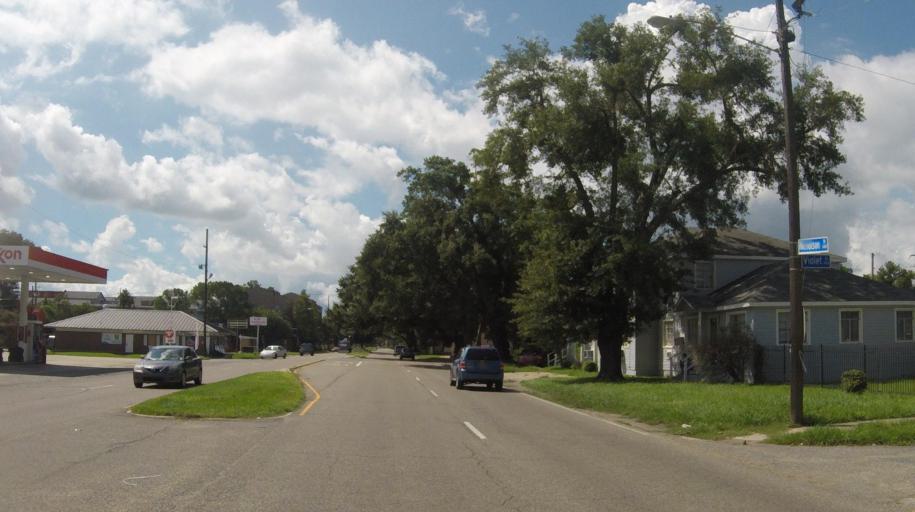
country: US
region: Louisiana
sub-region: West Baton Rouge Parish
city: Port Allen
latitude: 30.4204
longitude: -91.1876
